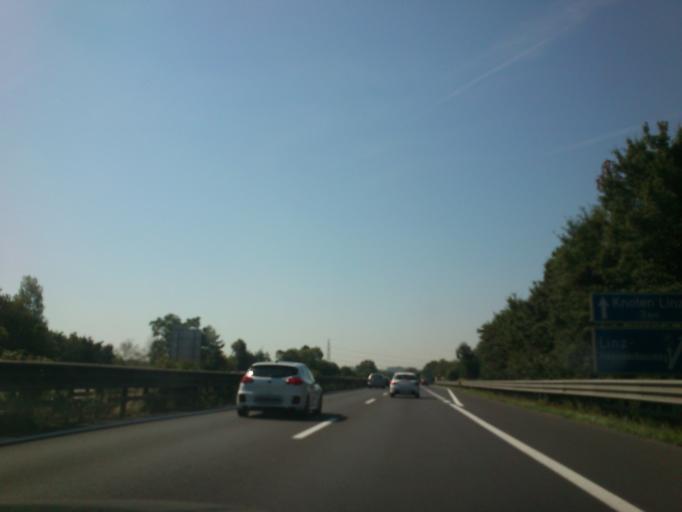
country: AT
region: Upper Austria
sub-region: Politischer Bezirk Linz-Land
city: Ansfelden
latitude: 48.2475
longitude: 14.2972
